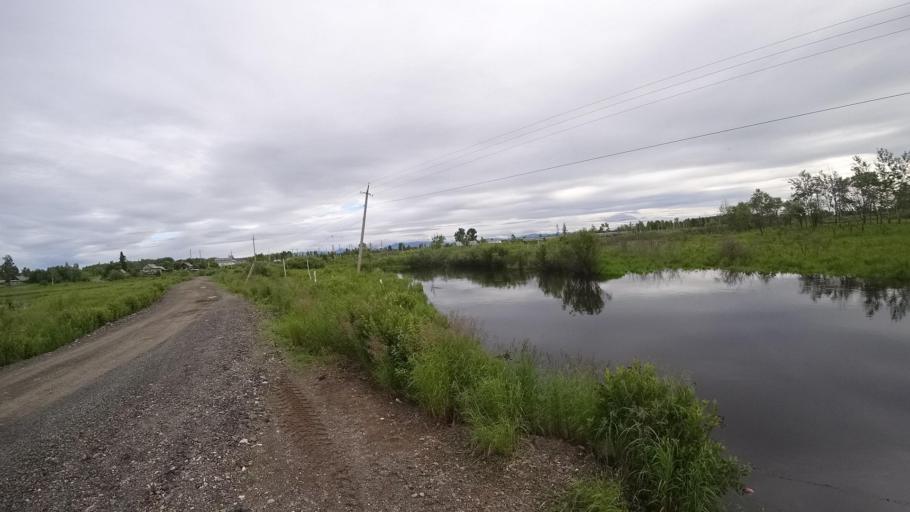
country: RU
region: Khabarovsk Krai
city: Amursk
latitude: 49.9016
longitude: 136.1474
